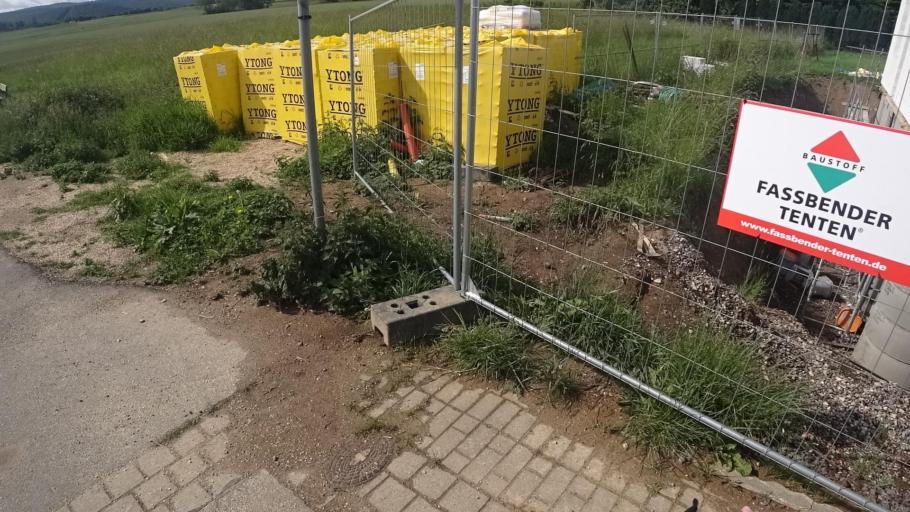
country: DE
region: Rheinland-Pfalz
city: Dernau
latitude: 50.5496
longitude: 7.0380
